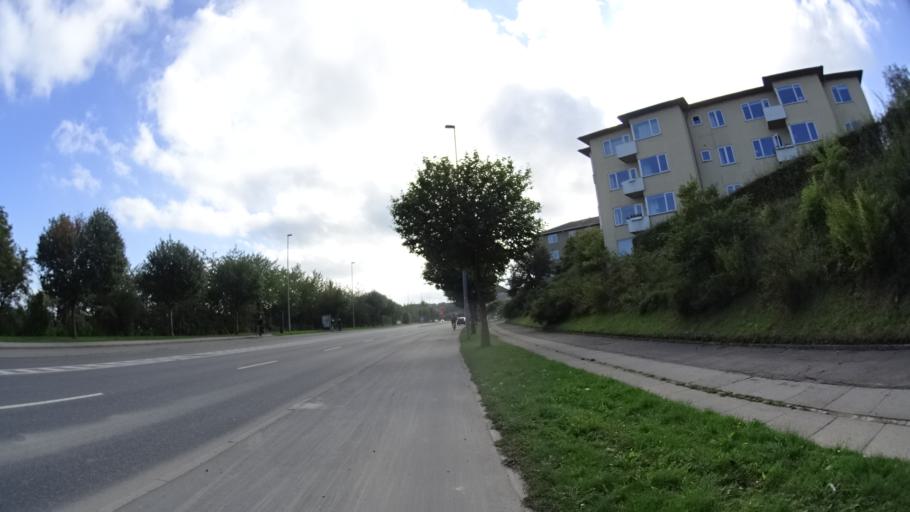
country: DK
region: Central Jutland
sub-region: Arhus Kommune
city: Arhus
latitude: 56.1444
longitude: 10.2085
